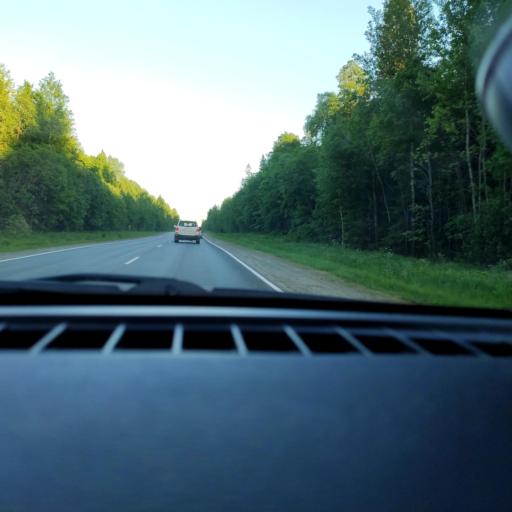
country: RU
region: Perm
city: Perm
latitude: 58.1841
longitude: 56.2215
